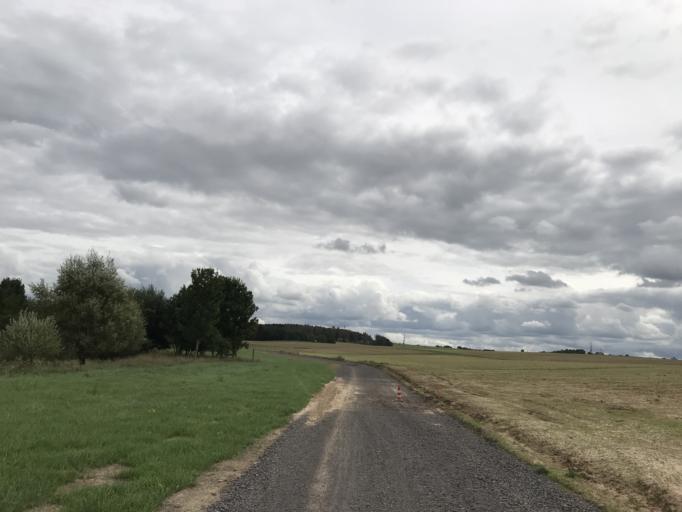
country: DE
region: Hesse
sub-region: Regierungsbezirk Giessen
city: Grunberg
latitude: 50.6317
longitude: 8.9505
